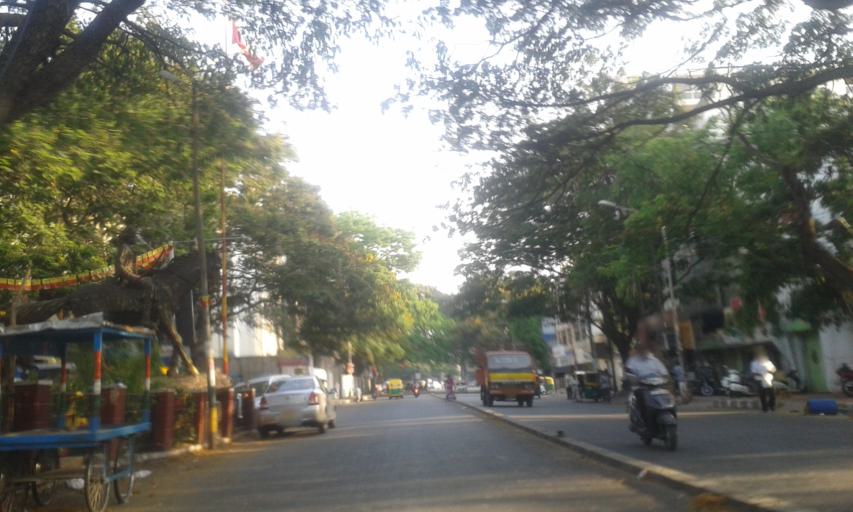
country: IN
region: Karnataka
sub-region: Bangalore Urban
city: Bangalore
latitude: 12.9501
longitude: 77.5801
